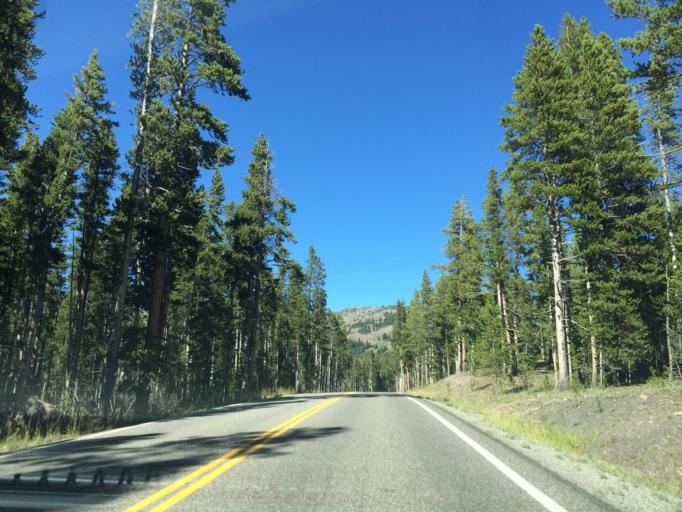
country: US
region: Montana
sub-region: Gallatin County
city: West Yellowstone
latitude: 44.7465
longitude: -110.4941
